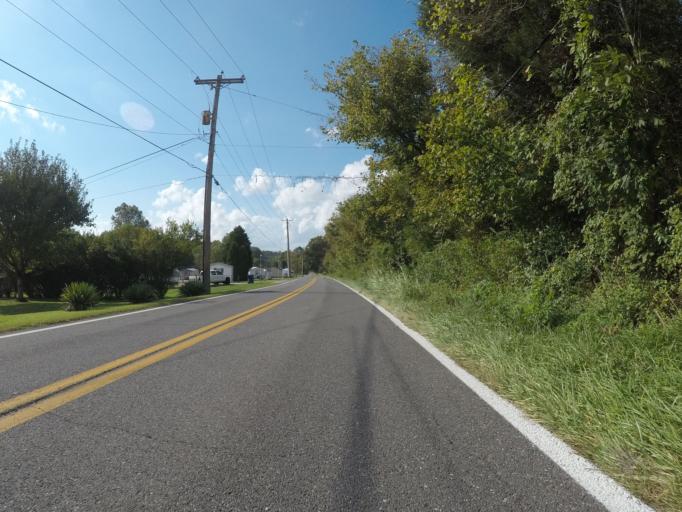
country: US
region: West Virginia
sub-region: Wayne County
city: Lavalette
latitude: 38.3517
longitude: -82.4993
